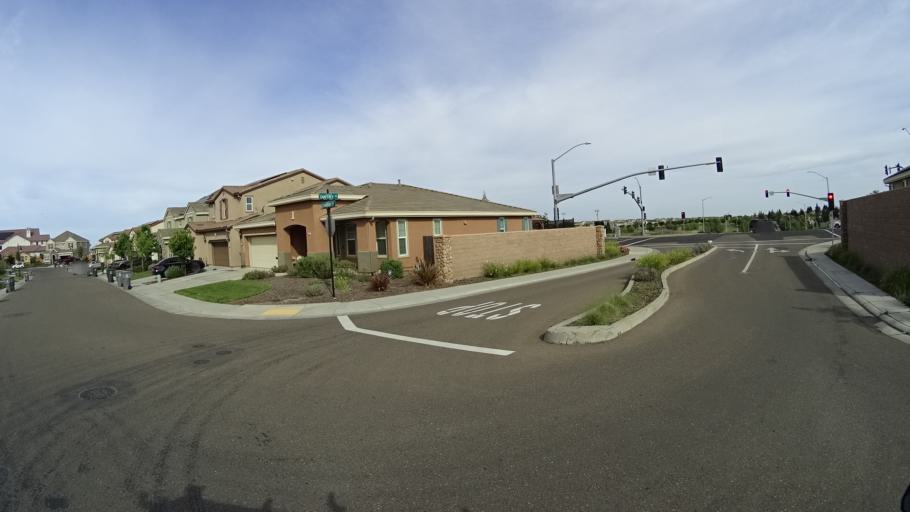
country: US
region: California
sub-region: Placer County
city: Rocklin
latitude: 38.8179
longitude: -121.2806
